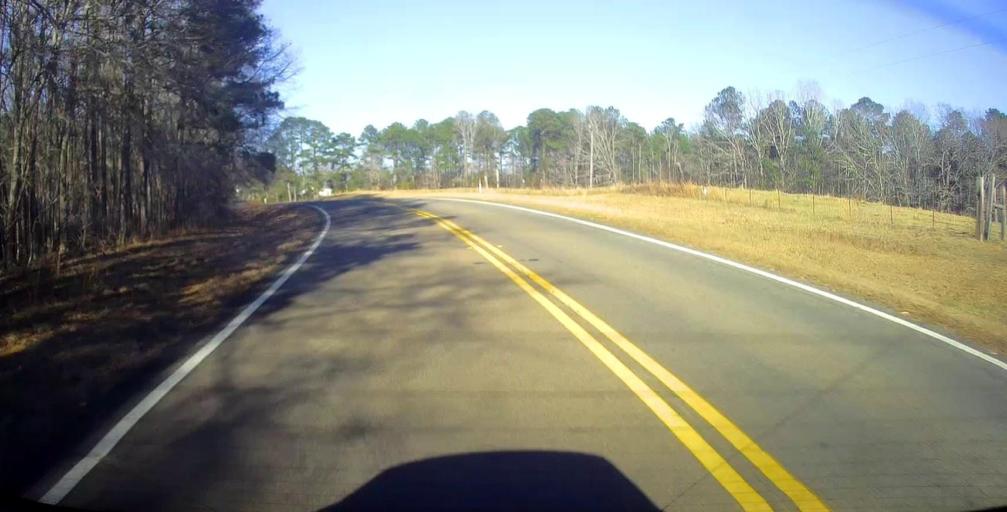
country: US
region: Georgia
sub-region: Talbot County
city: Sardis
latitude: 32.7862
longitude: -84.6455
